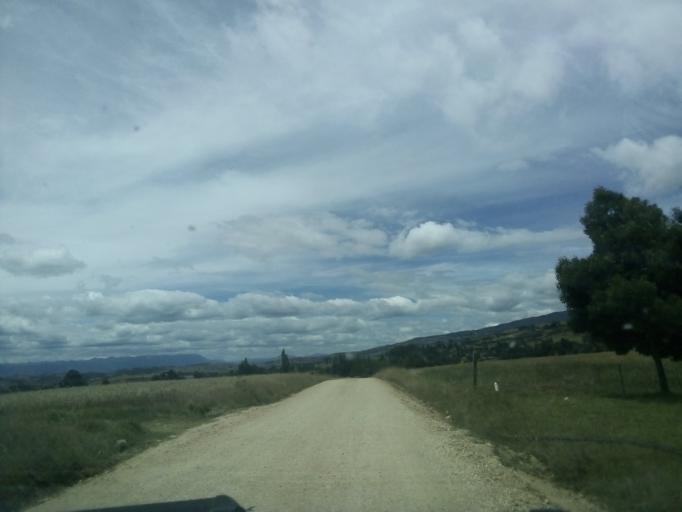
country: CO
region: Boyaca
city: Toca
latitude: 5.5893
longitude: -73.1664
